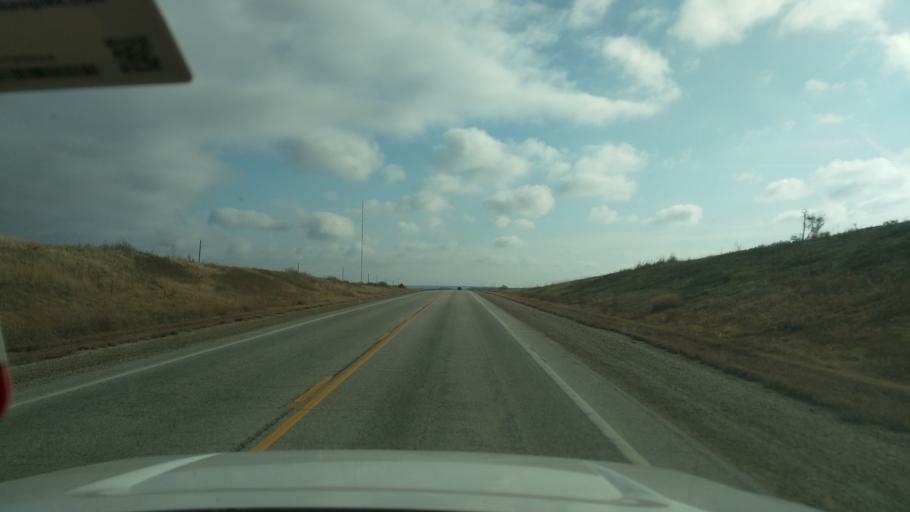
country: US
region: Kansas
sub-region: Chautauqua County
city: Sedan
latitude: 37.0834
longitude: -96.1972
